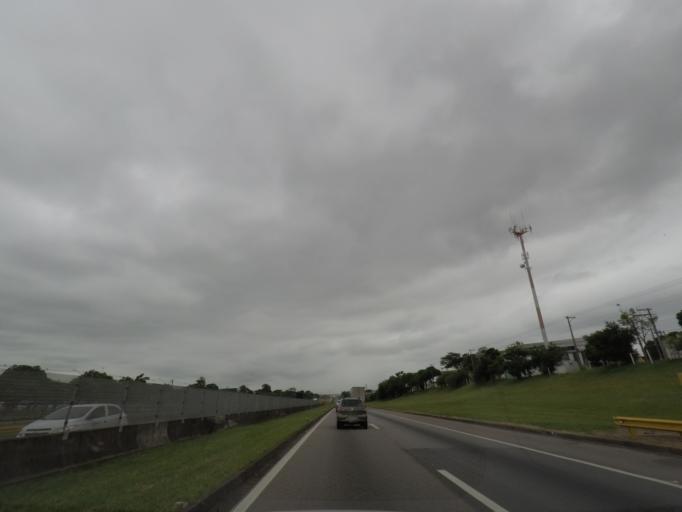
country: BR
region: Sao Paulo
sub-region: Sao Jose Dos Campos
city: Sao Jose dos Campos
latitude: -23.1718
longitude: -45.8246
